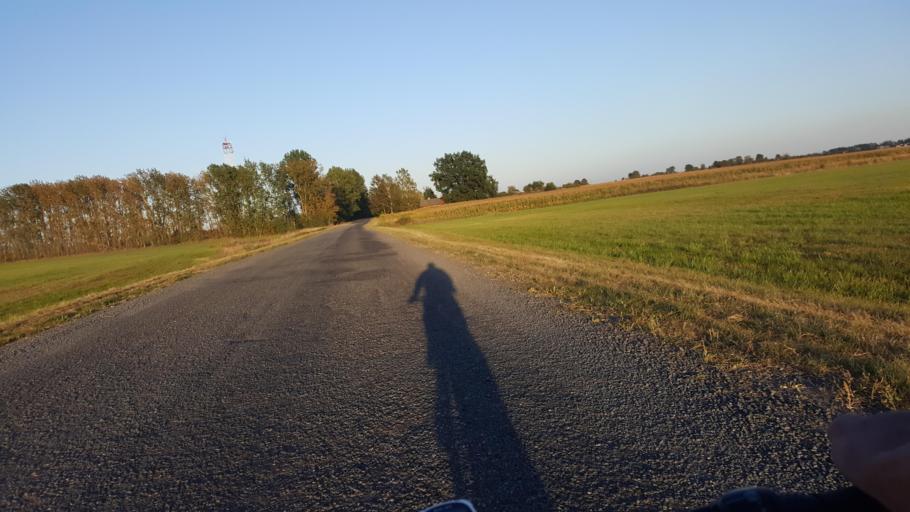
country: BY
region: Brest
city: Vysokaye
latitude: 52.2975
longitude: 23.5109
